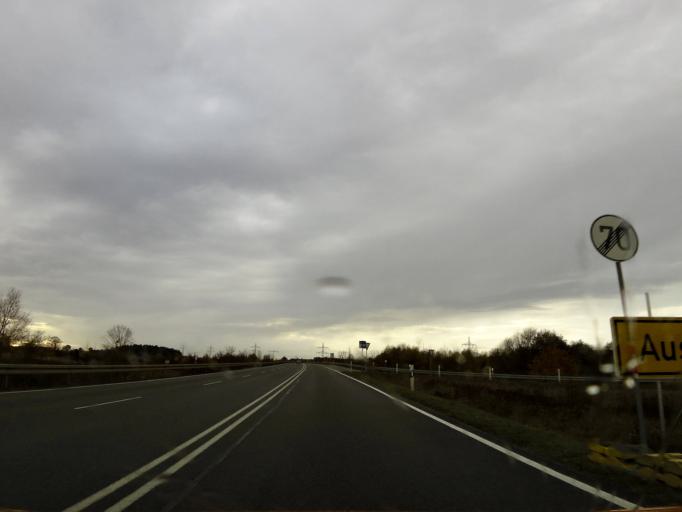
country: DE
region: Saxony-Anhalt
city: Gardelegen
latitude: 52.5377
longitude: 11.3764
